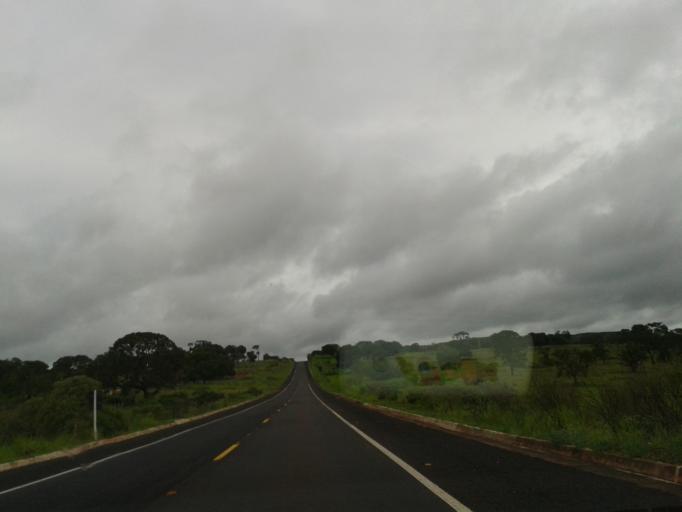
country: BR
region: Minas Gerais
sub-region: Santa Vitoria
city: Santa Vitoria
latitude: -19.2401
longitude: -50.0151
